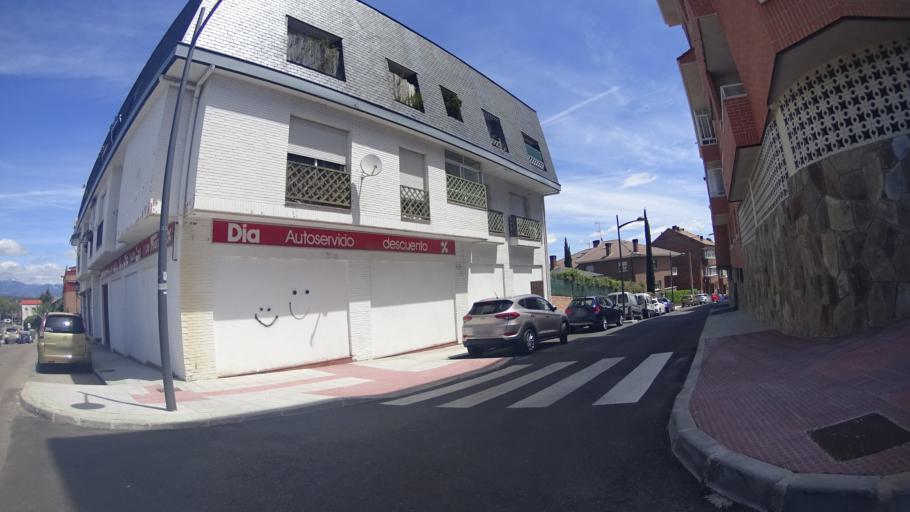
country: ES
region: Madrid
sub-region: Provincia de Madrid
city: Galapagar
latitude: 40.5798
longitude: -4.0078
